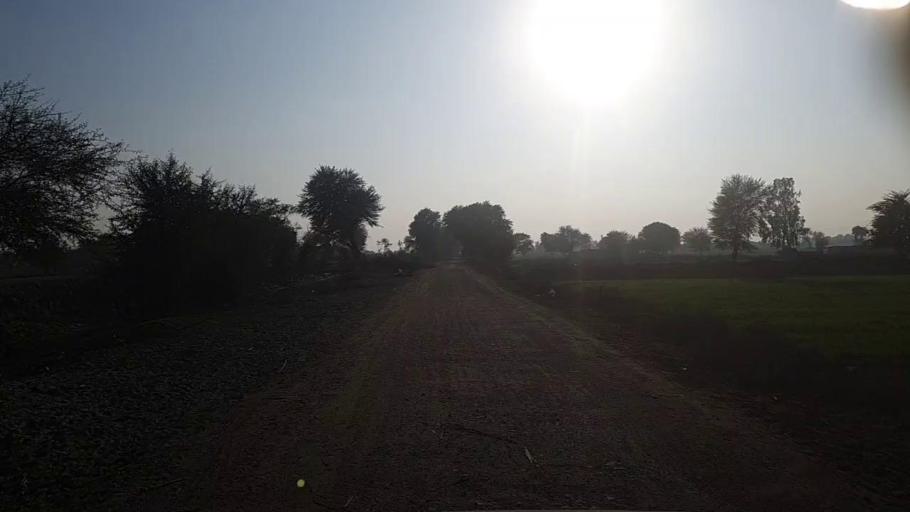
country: PK
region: Sindh
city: Khairpur
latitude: 28.0758
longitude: 69.7364
